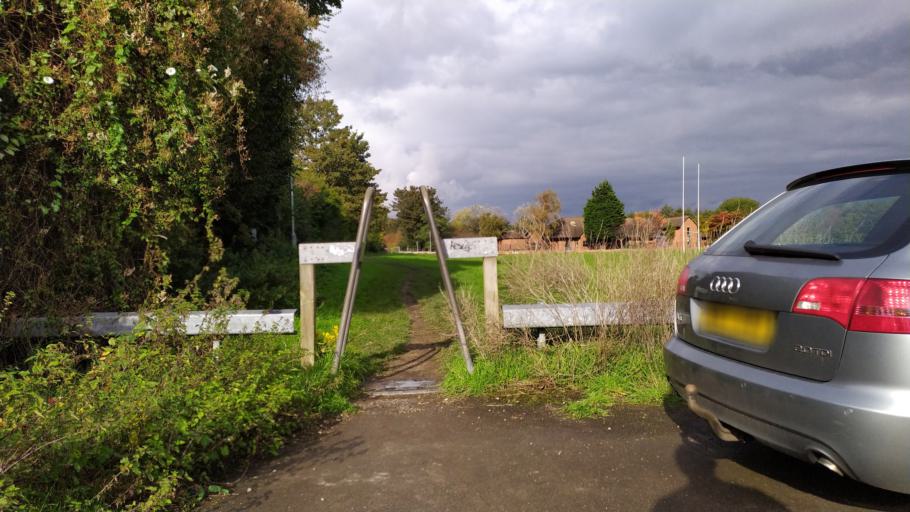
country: GB
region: England
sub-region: City and Borough of Leeds
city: Chapel Allerton
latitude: 53.8221
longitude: -1.5473
